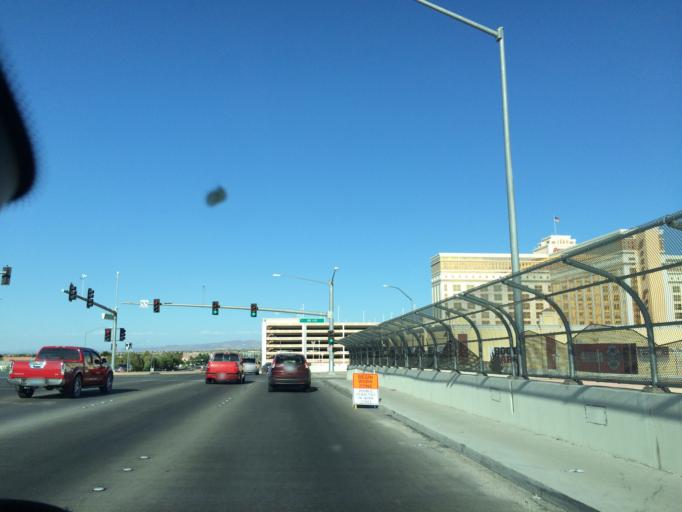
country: US
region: Nevada
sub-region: Clark County
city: Enterprise
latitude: 36.0129
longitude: -115.1805
